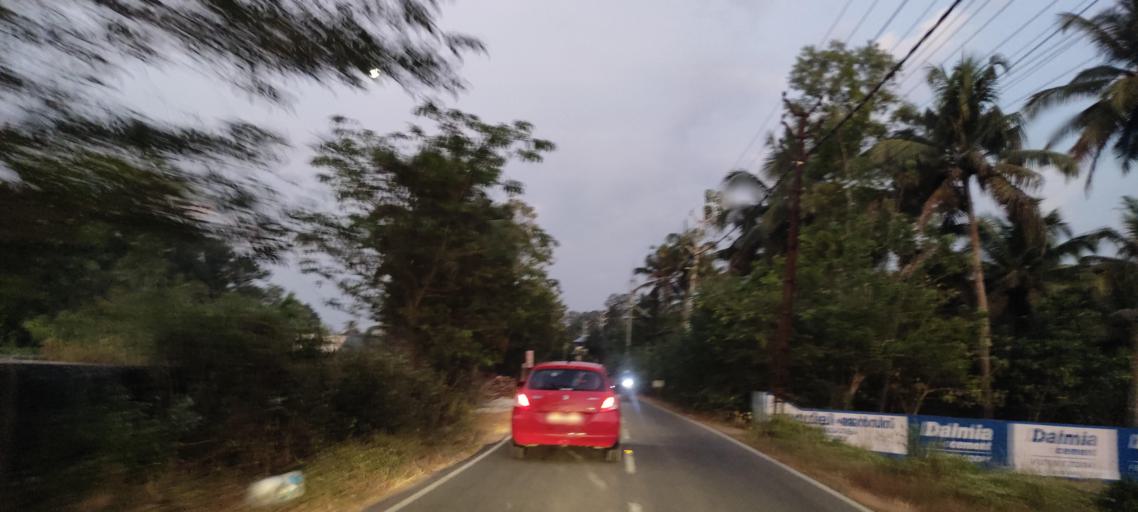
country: IN
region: Kerala
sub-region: Alappuzha
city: Kutiatodu
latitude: 9.7739
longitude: 76.3574
